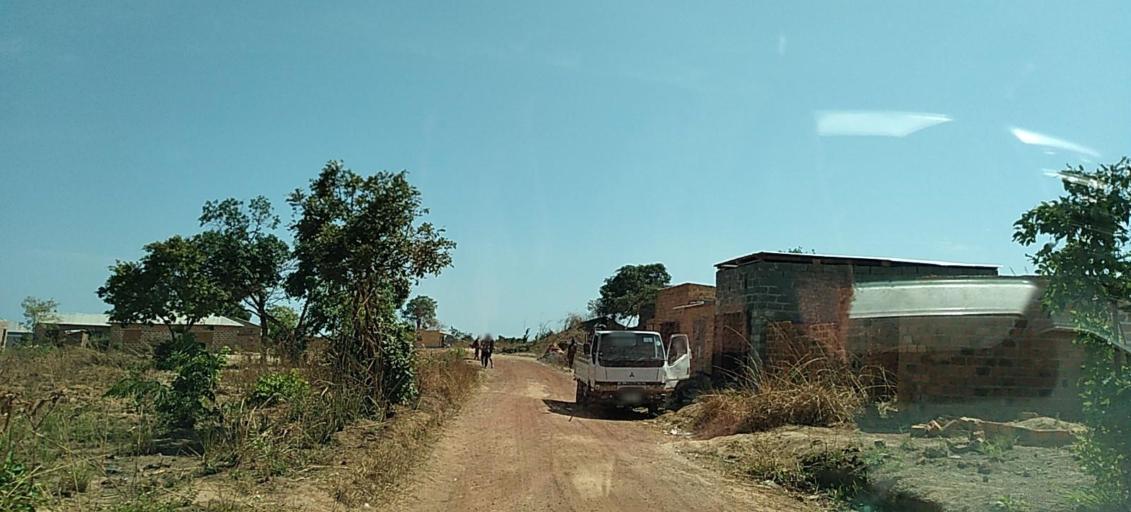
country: ZM
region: Copperbelt
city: Chililabombwe
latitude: -12.3191
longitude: 27.8622
